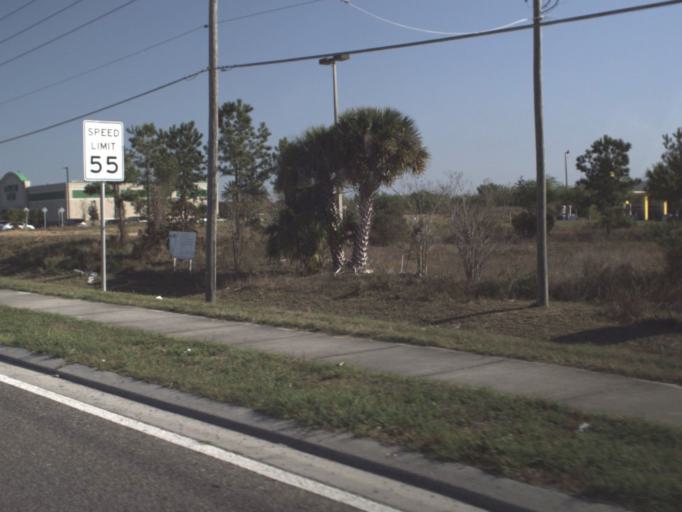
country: US
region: Florida
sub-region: Lake County
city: Four Corners
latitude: 28.3648
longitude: -81.6810
